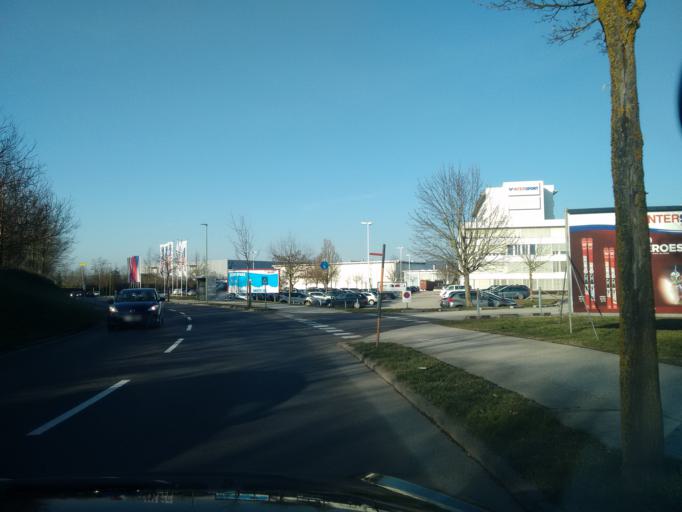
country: AT
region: Upper Austria
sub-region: Wels Stadt
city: Wels
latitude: 48.1753
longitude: 14.0433
